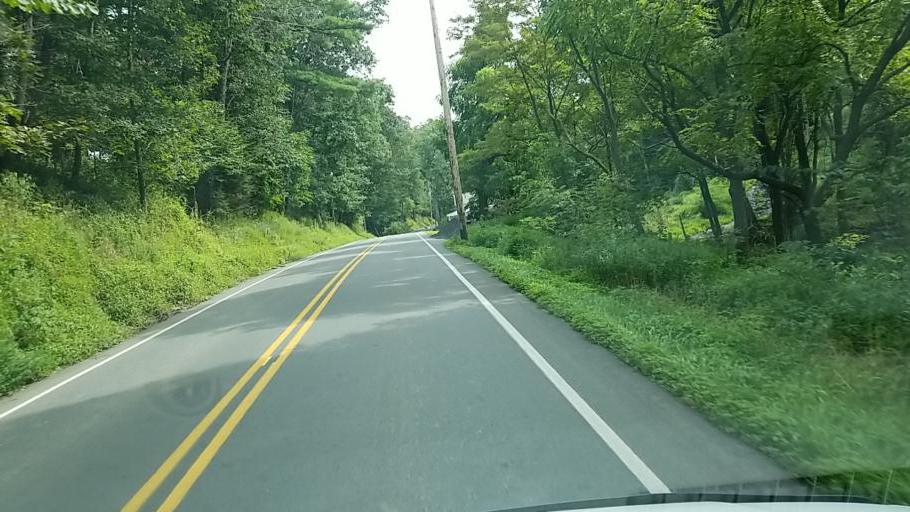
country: US
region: Pennsylvania
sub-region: Dauphin County
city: Elizabethville
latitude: 40.6247
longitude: -76.7863
